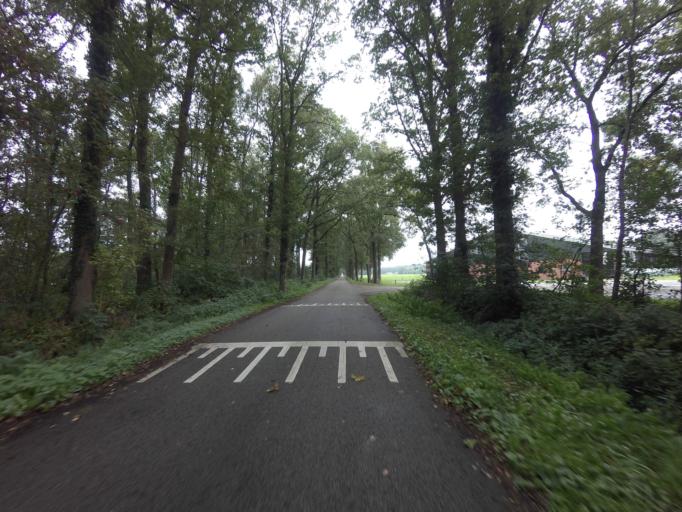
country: NL
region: Overijssel
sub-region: Gemeente Enschede
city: Enschede
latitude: 52.1894
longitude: 6.9293
